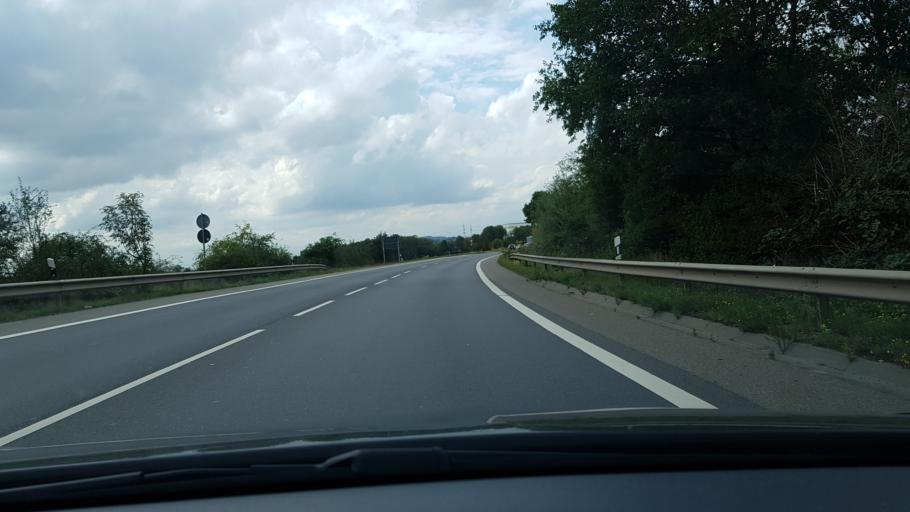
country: DE
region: Rheinland-Pfalz
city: Andernach
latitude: 50.4221
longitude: 7.4258
